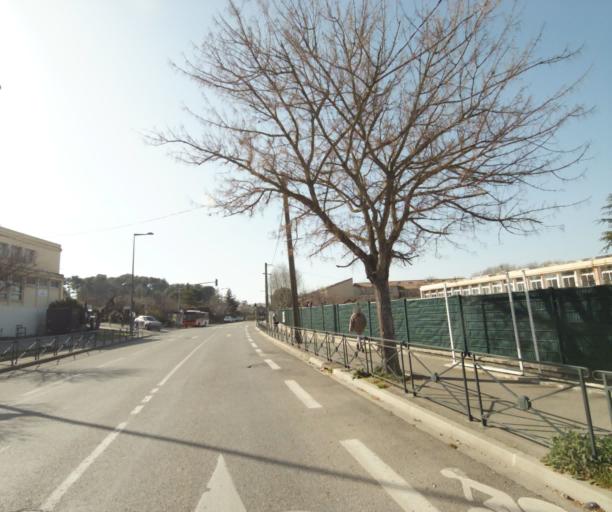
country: FR
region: Provence-Alpes-Cote d'Azur
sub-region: Departement des Bouches-du-Rhone
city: Aix-en-Provence
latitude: 43.5097
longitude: 5.4391
